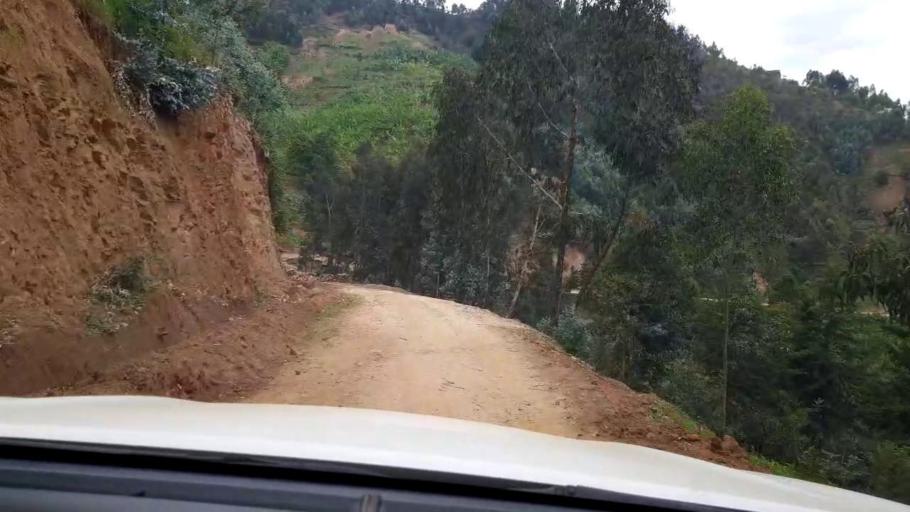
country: RW
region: Western Province
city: Kibuye
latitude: -1.8270
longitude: 29.5461
